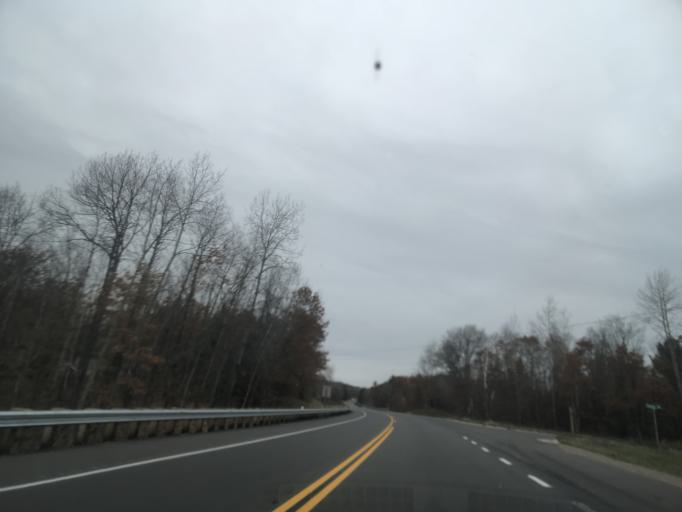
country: US
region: Wisconsin
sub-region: Menominee County
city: Legend Lake
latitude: 45.2722
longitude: -88.5086
